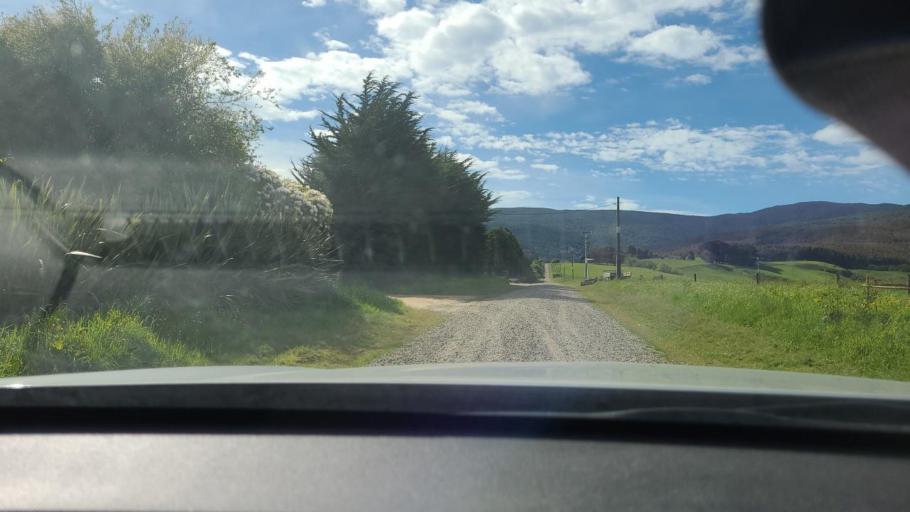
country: NZ
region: Southland
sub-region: Southland District
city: Riverton
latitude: -46.1371
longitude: 167.7728
